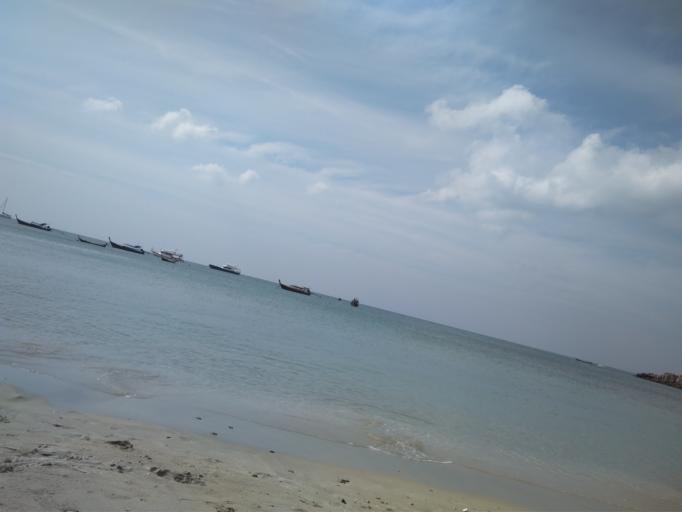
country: TH
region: Krabi
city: Ko Lanta
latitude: 7.4980
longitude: 99.0723
